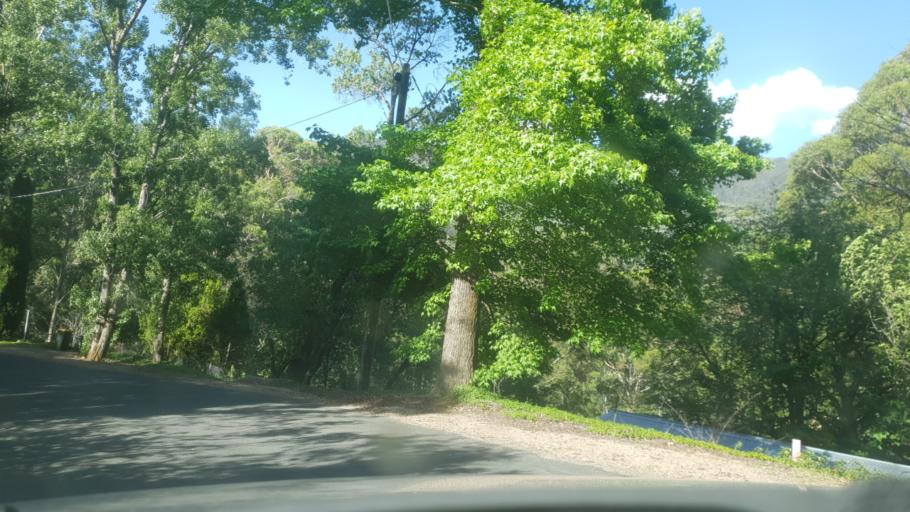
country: AU
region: Victoria
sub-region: Alpine
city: Mount Beauty
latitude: -36.8047
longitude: 147.2271
